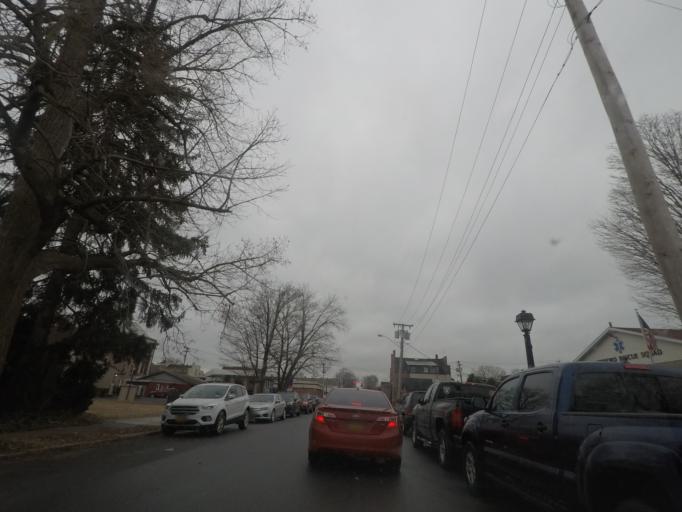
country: US
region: New York
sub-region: Saratoga County
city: Waterford
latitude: 42.7914
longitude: -73.6789
